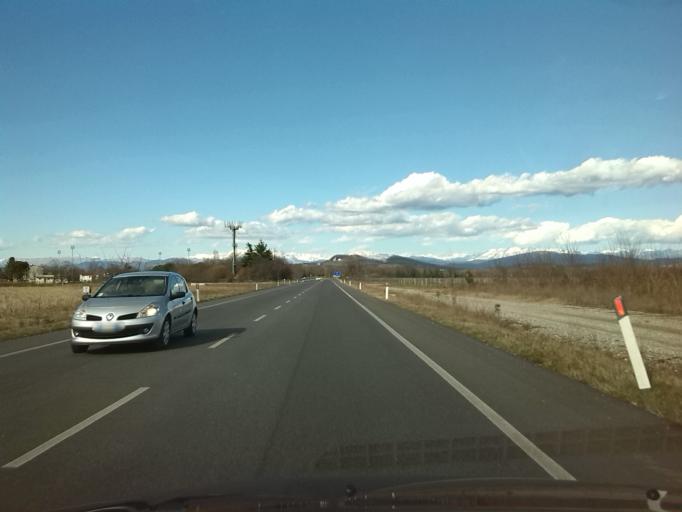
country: IT
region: Friuli Venezia Giulia
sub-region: Provincia di Gorizia
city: Mariano del Friuli
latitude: 45.9144
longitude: 13.4681
